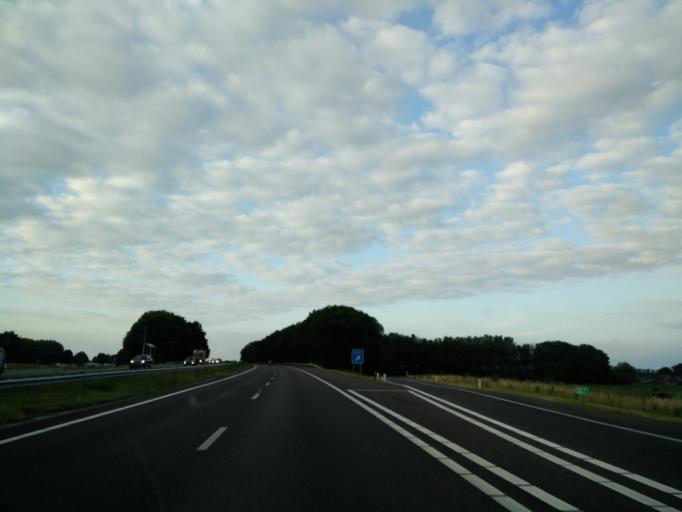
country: NL
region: Gelderland
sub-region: Gemeente Nijkerk
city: Nijkerk
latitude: 52.2639
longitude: 5.5327
